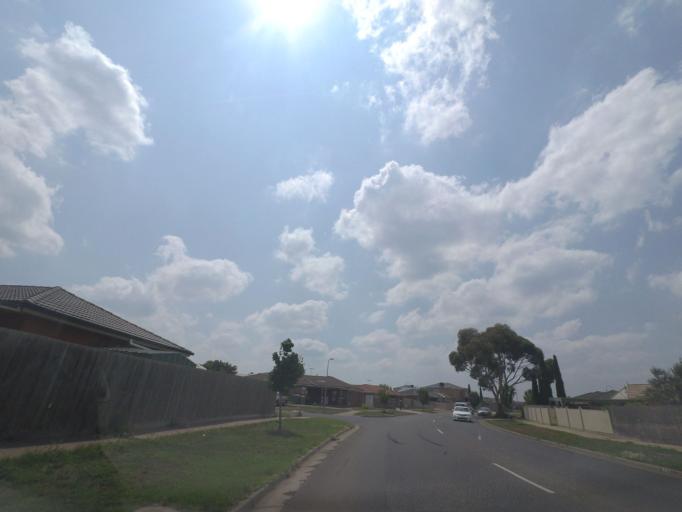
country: AU
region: Victoria
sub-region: Melton
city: Melton West
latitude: -37.6704
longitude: 144.5560
